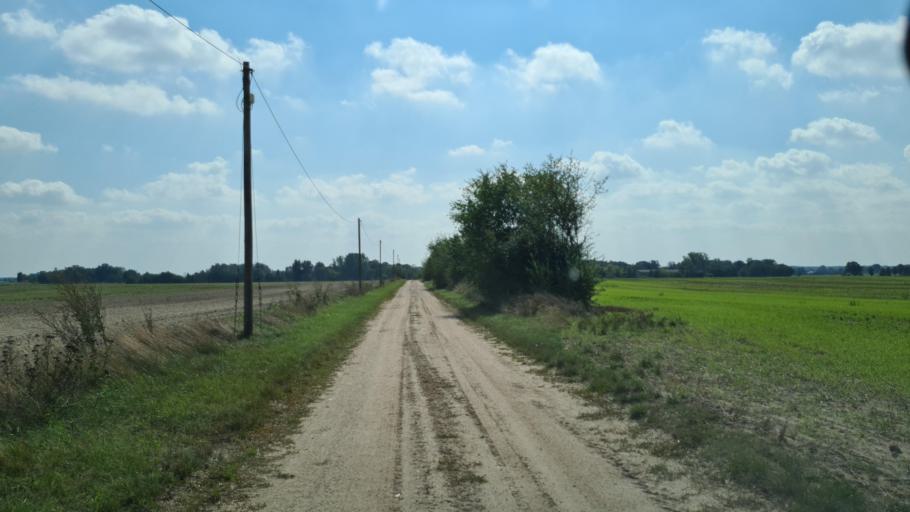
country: DE
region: Brandenburg
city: Sonnewalde
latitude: 51.7256
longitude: 13.6503
